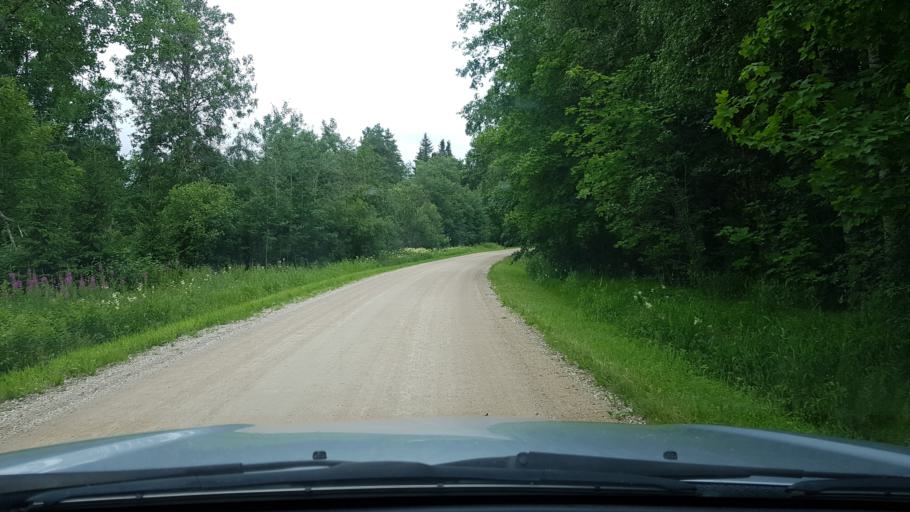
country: EE
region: Ida-Virumaa
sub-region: Narva-Joesuu linn
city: Narva-Joesuu
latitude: 59.3585
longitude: 28.0408
